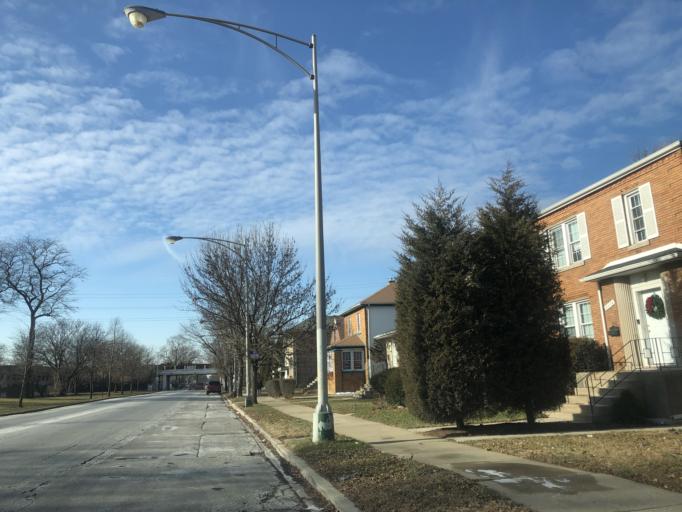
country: US
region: Illinois
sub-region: Cook County
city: Hometown
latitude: 41.7716
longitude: -87.7108
